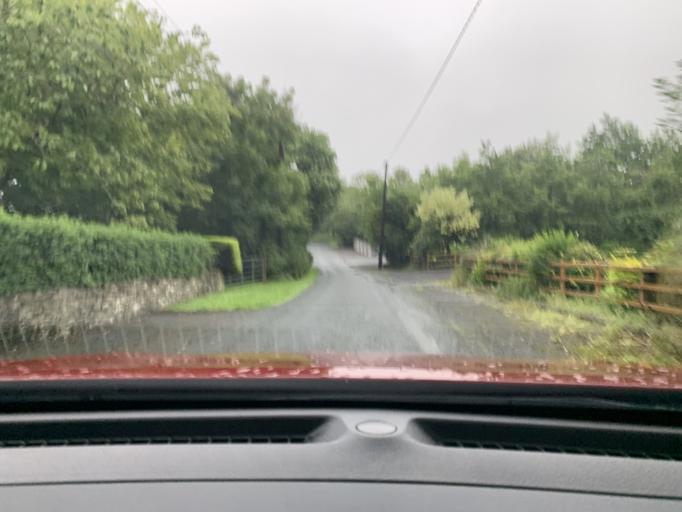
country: IE
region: Connaught
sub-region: Sligo
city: Sligo
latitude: 54.3191
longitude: -8.4576
